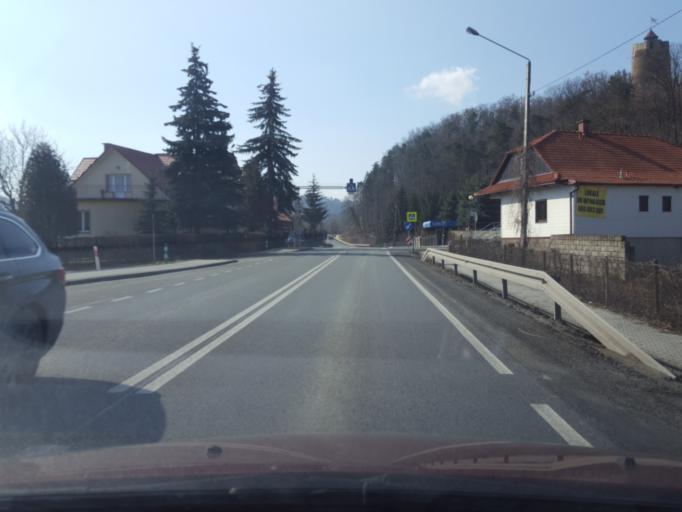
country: PL
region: Lesser Poland Voivodeship
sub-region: Powiat brzeski
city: Czchow
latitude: 49.8350
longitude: 20.6795
